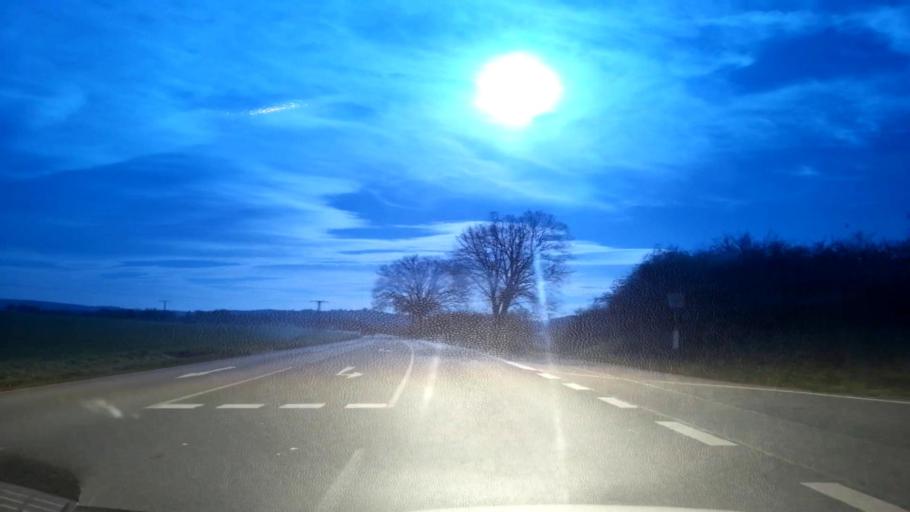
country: DE
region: Bavaria
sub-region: Upper Franconia
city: Reuth
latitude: 49.9550
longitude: 11.7049
